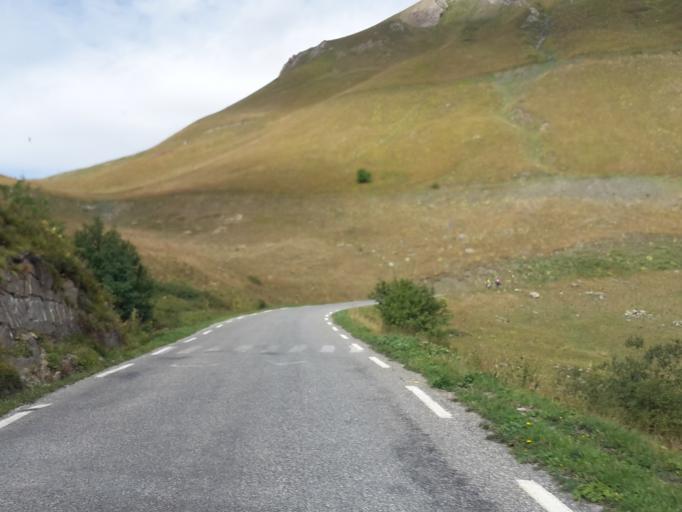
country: FR
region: Provence-Alpes-Cote d'Azur
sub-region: Departement des Hautes-Alpes
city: Le Monetier-les-Bains
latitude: 45.0384
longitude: 6.4020
